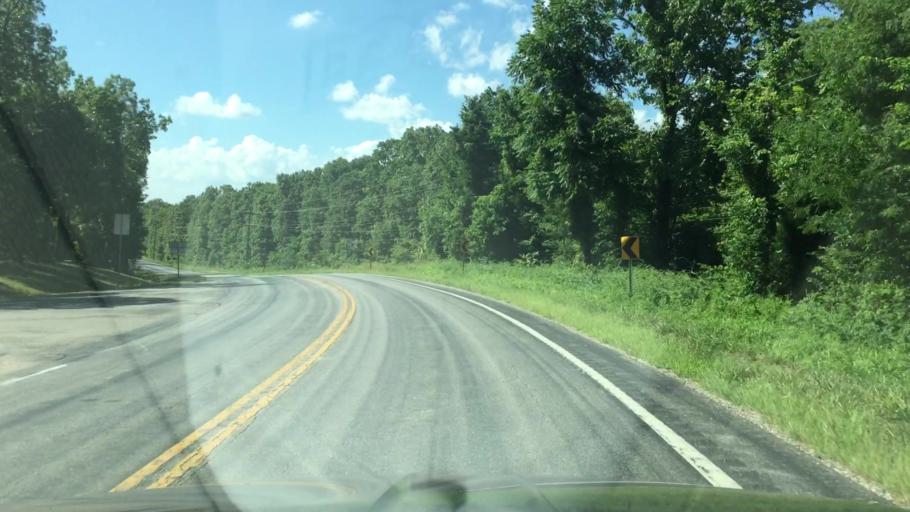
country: US
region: Missouri
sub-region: Camden County
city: Osage Beach
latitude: 38.1303
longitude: -92.5571
